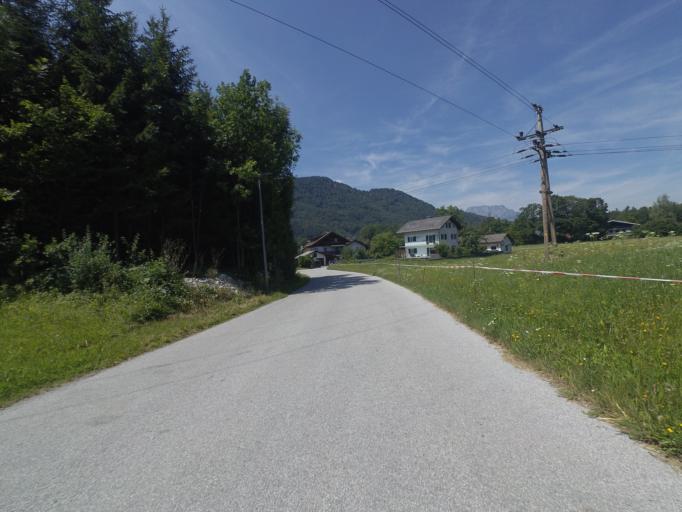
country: AT
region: Salzburg
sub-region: Politischer Bezirk Hallein
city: Adnet
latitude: 47.6538
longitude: 13.1316
